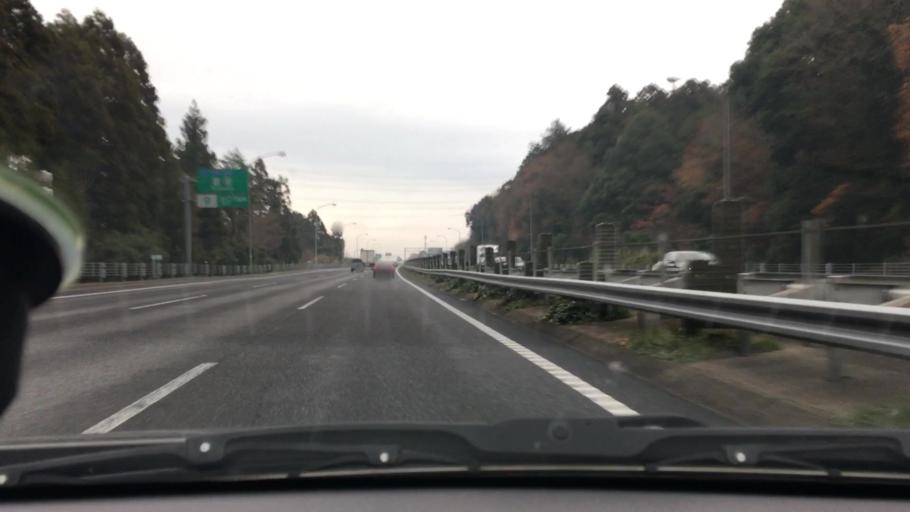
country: JP
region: Chiba
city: Shisui
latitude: 35.7365
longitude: 140.3018
